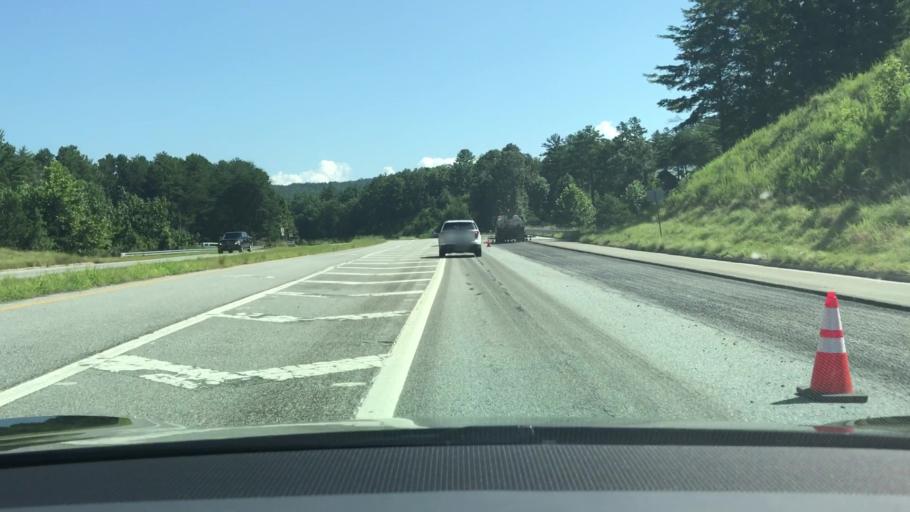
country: US
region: Georgia
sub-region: Rabun County
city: Clayton
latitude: 34.7517
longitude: -83.3983
